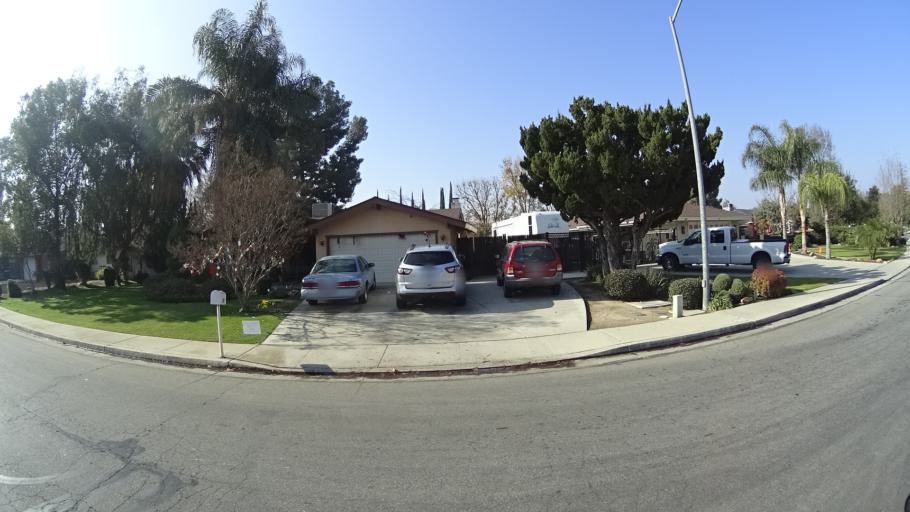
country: US
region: California
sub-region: Kern County
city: Greenacres
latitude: 35.3566
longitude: -119.0863
